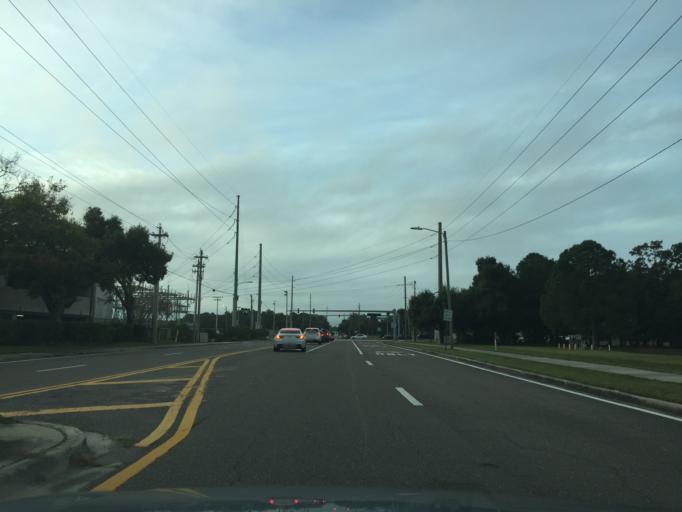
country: US
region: Florida
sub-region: Hillsborough County
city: Town 'n' Country
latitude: 27.9781
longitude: -82.5507
